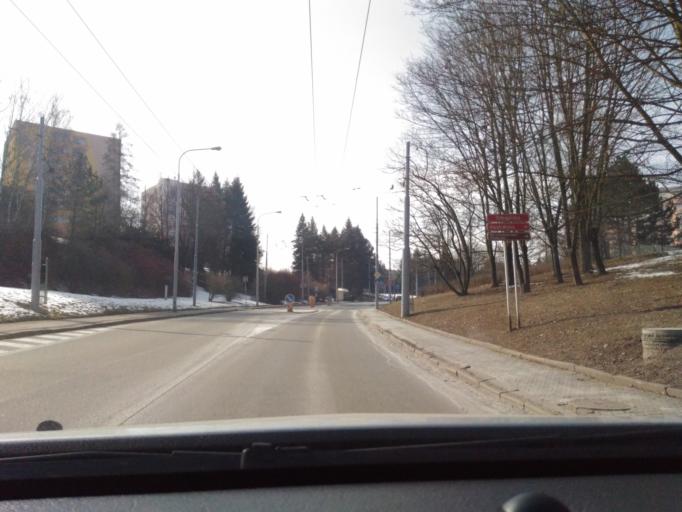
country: CZ
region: South Moravian
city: Troubsko
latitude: 49.2222
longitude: 16.5299
